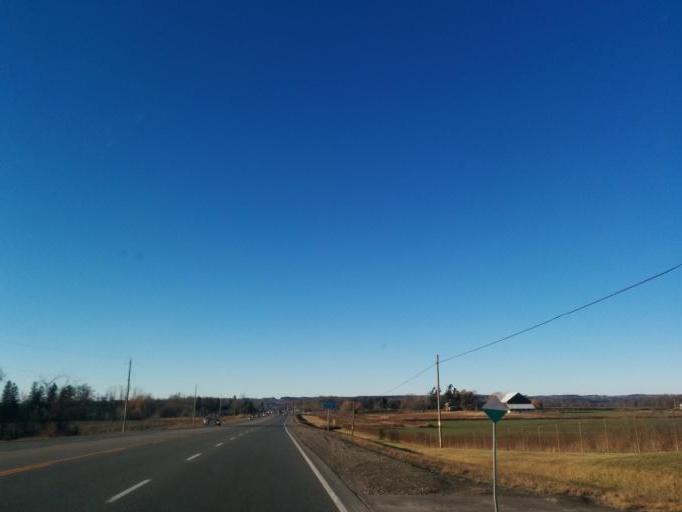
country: CA
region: Ontario
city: Brampton
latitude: 43.7965
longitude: -79.9095
